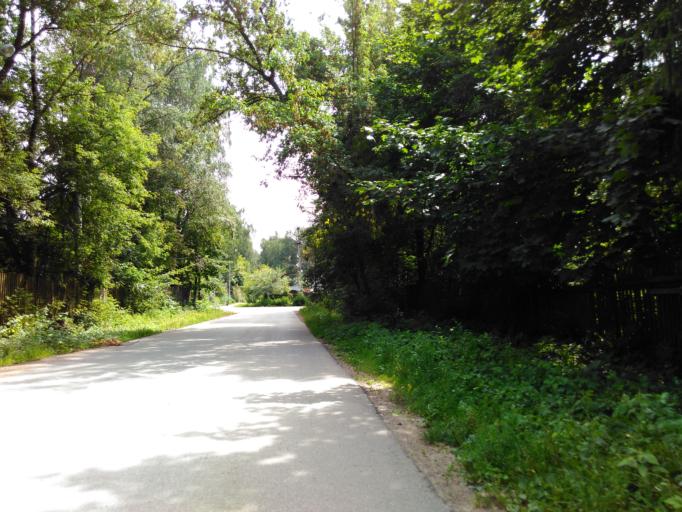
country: RU
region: Moskovskaya
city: Pravdinskiy
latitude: 56.0514
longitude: 37.8463
